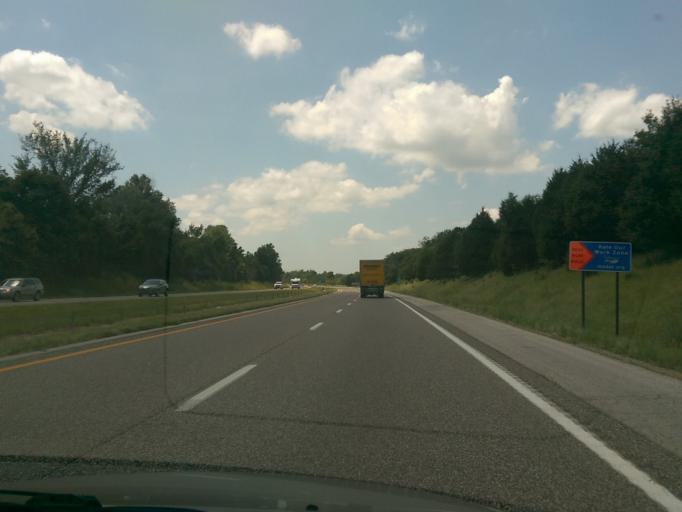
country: US
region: Missouri
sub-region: Boone County
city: Columbia
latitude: 38.9742
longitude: -92.5129
